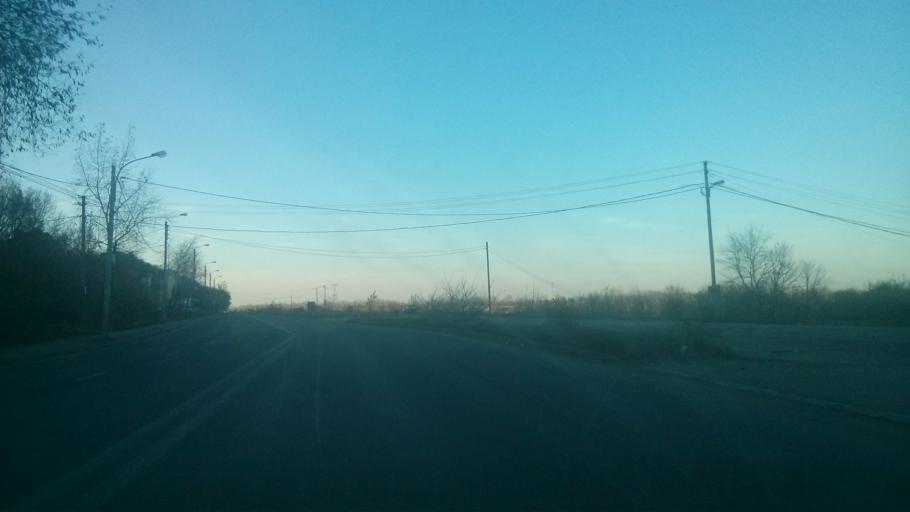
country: RU
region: Nizjnij Novgorod
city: Bor
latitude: 56.3170
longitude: 44.0803
